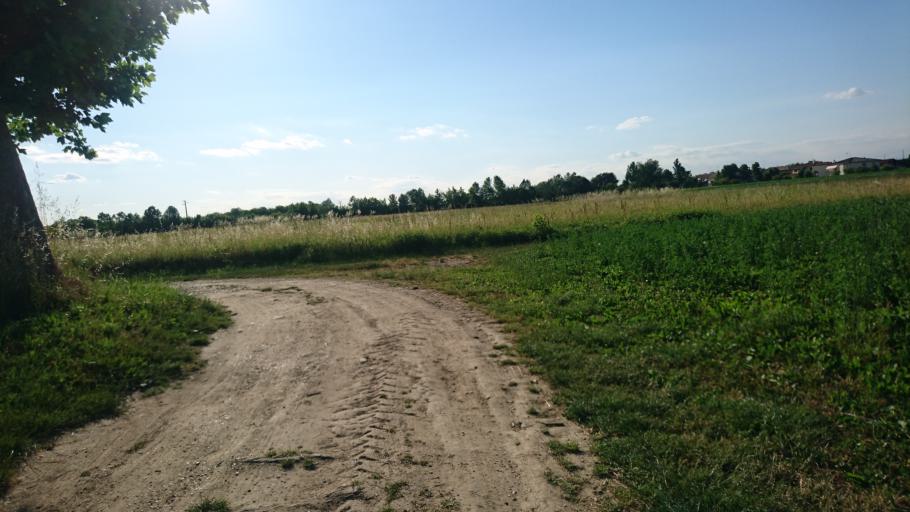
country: IT
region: Veneto
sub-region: Provincia di Padova
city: Ponte San Nicolo
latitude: 45.3617
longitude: 11.9229
